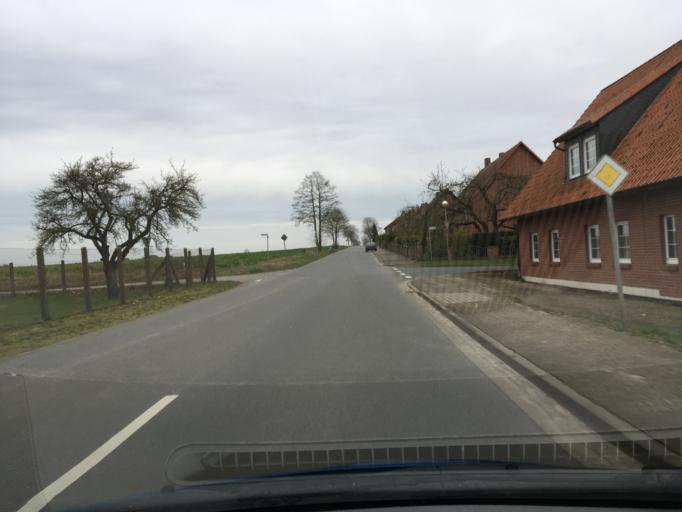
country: DE
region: Lower Saxony
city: Emmendorf
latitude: 53.0043
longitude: 10.6131
